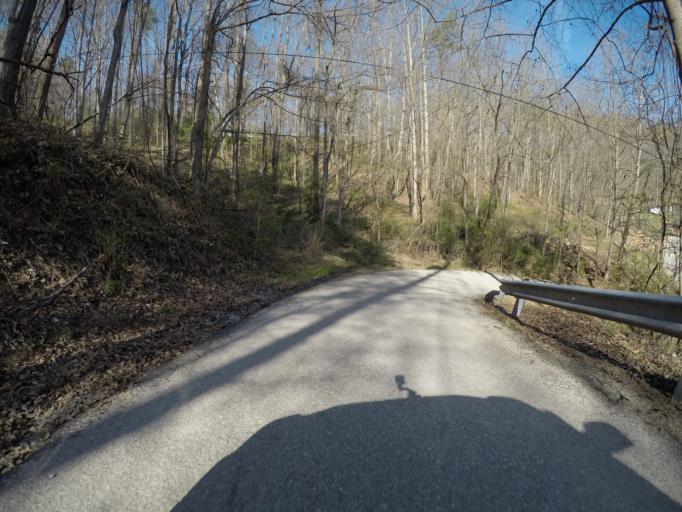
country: US
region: West Virginia
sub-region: Kanawha County
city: Charleston
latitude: 38.3808
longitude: -81.6061
